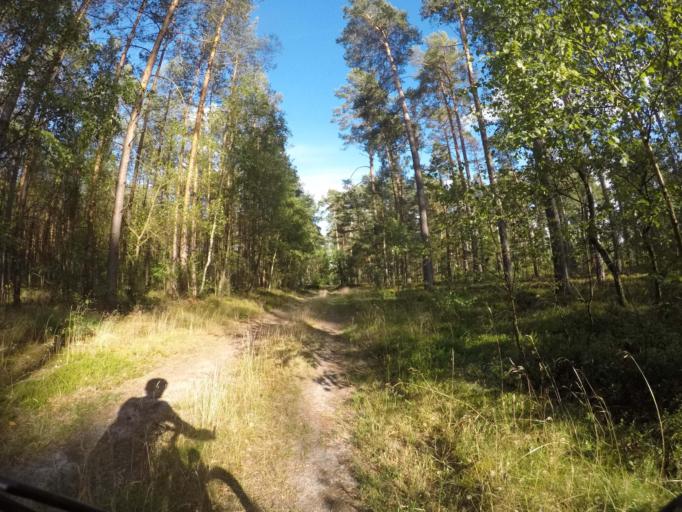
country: DE
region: Mecklenburg-Vorpommern
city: Lubtheen
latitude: 53.2453
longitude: 11.0122
